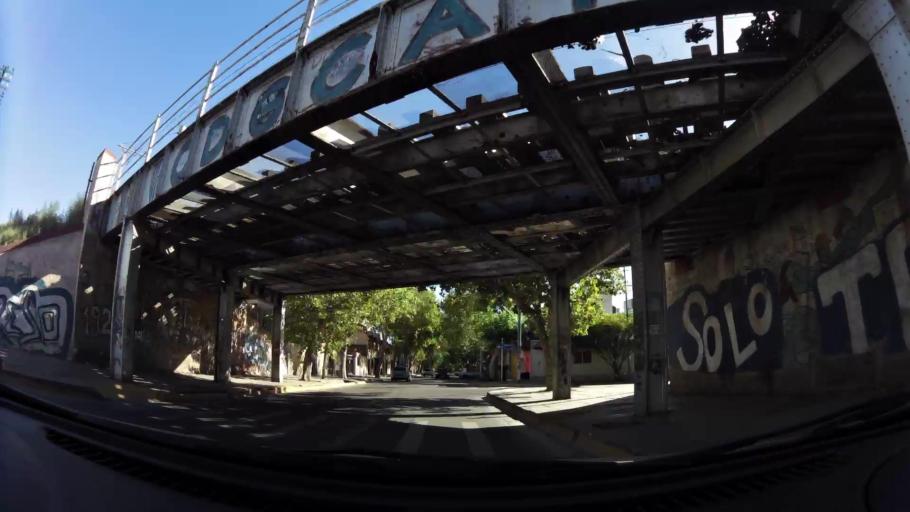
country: AR
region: Mendoza
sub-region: Departamento de Godoy Cruz
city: Godoy Cruz
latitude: -32.9186
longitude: -68.8433
